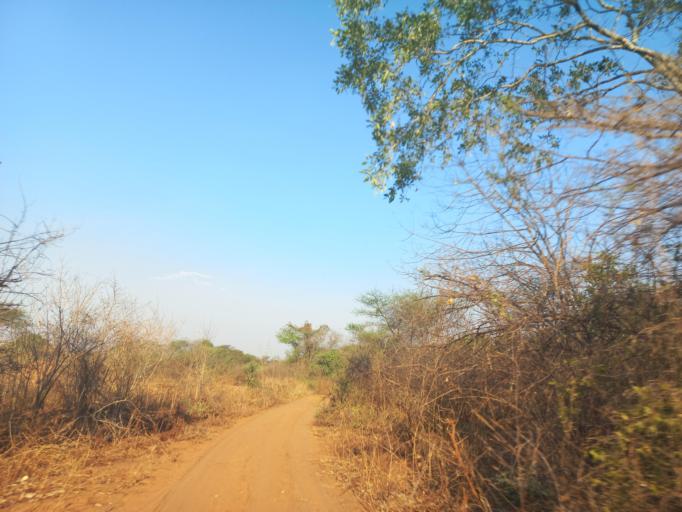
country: ZM
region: Lusaka
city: Luangwa
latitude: -15.4208
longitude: 30.2695
